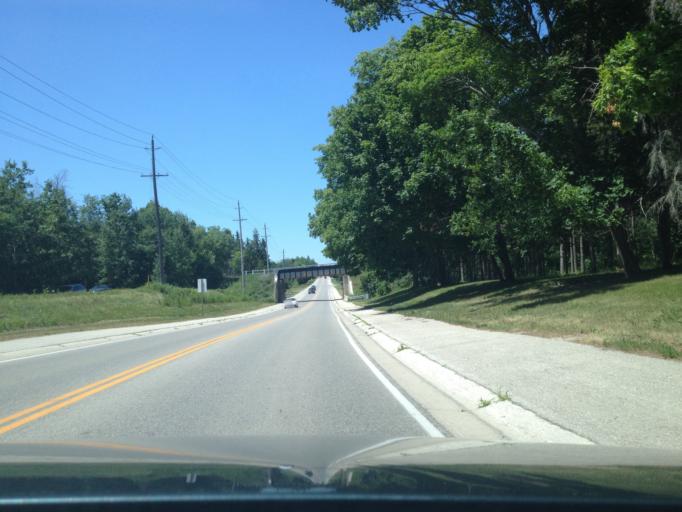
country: CA
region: Ontario
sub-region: Wellington County
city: Guelph
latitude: 43.6907
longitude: -80.3949
